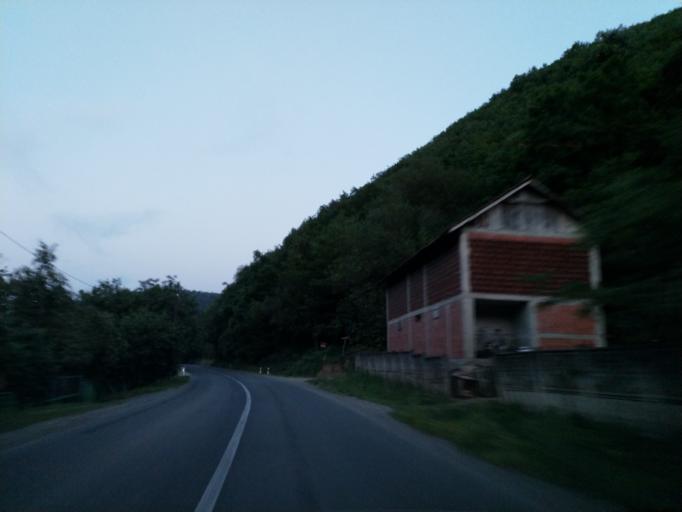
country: RS
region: Central Serbia
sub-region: Rasinski Okrug
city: Aleksandrovac
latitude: 43.3453
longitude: 21.1042
